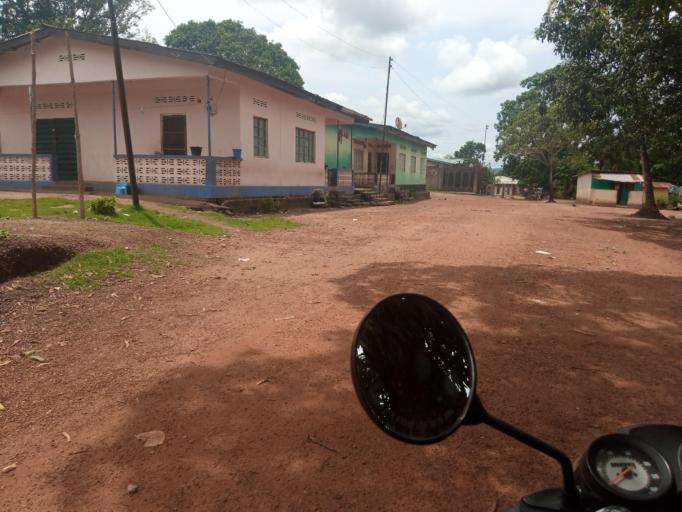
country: SL
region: Southern Province
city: Bo
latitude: 7.9532
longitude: -11.7186
